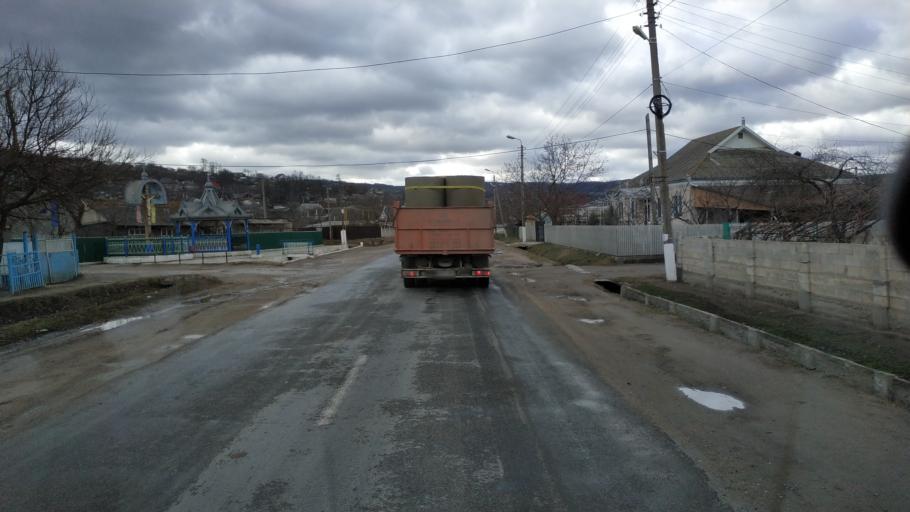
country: MD
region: Stinga Nistrului
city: Bucovat
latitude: 47.1601
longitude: 28.4338
